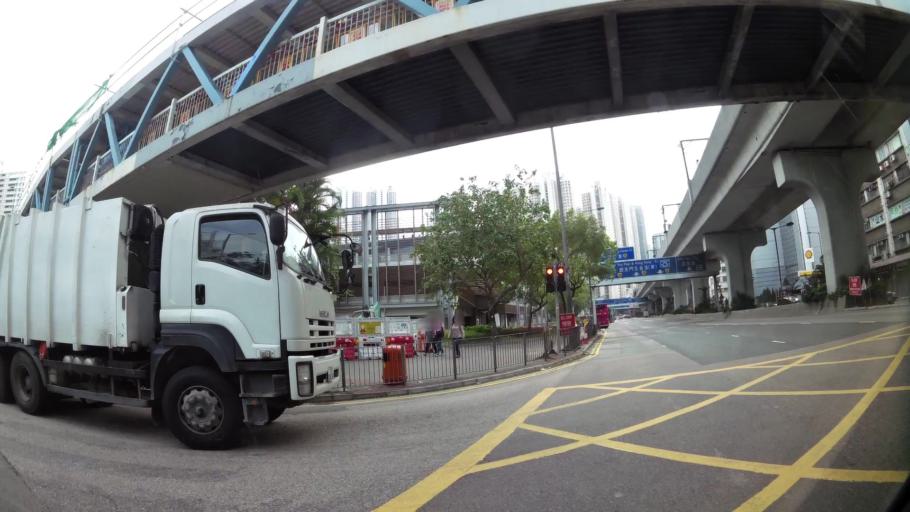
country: HK
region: Kowloon City
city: Kowloon
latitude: 22.3107
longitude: 114.2286
